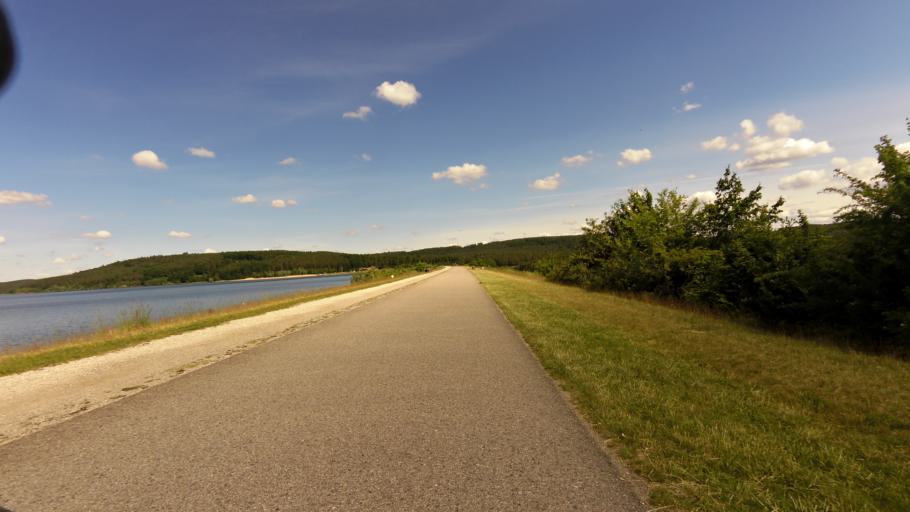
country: DE
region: Bavaria
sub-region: Regierungsbezirk Mittelfranken
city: Pleinfeld
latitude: 49.1243
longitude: 10.9644
